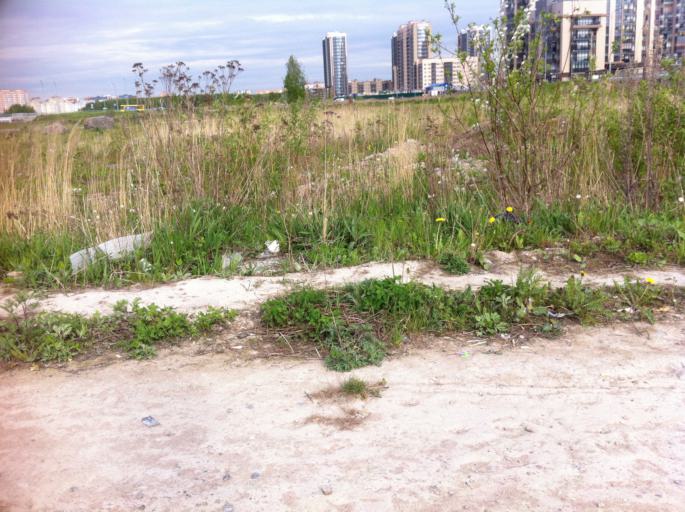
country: RU
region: St.-Petersburg
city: Sosnovaya Polyana
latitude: 59.8550
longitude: 30.1425
